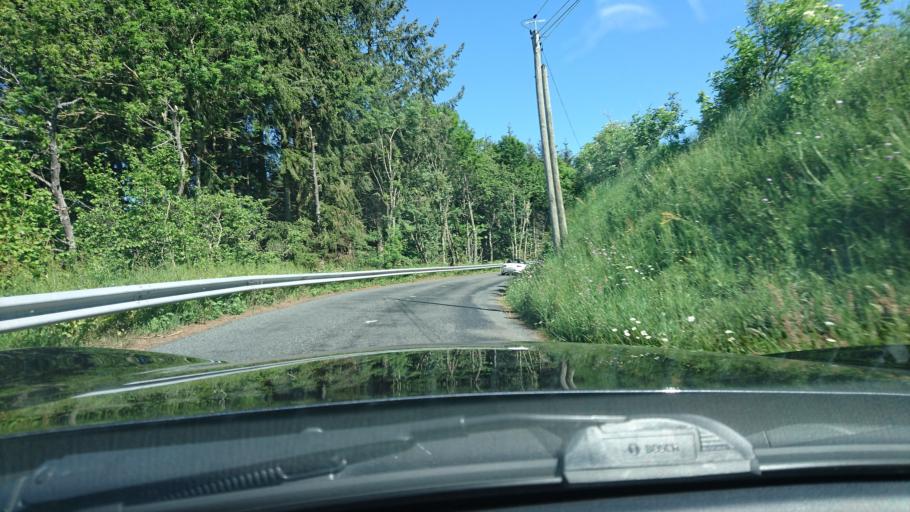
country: FR
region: Rhone-Alpes
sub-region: Departement de la Loire
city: Violay
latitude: 45.8466
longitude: 4.3634
